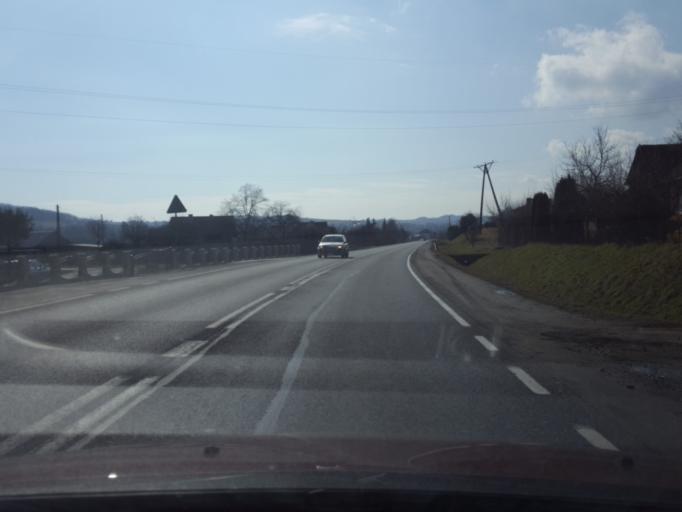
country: PL
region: Lesser Poland Voivodeship
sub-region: Powiat nowosadecki
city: Lososina Dolna
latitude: 49.7618
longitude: 20.6339
